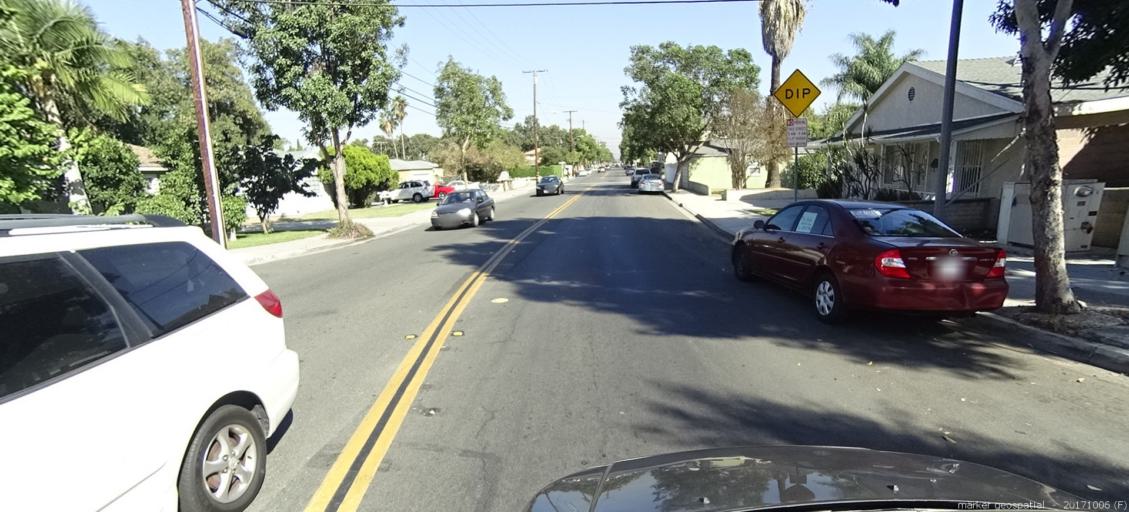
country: US
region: California
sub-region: Orange County
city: Garden Grove
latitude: 33.7814
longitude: -117.9406
